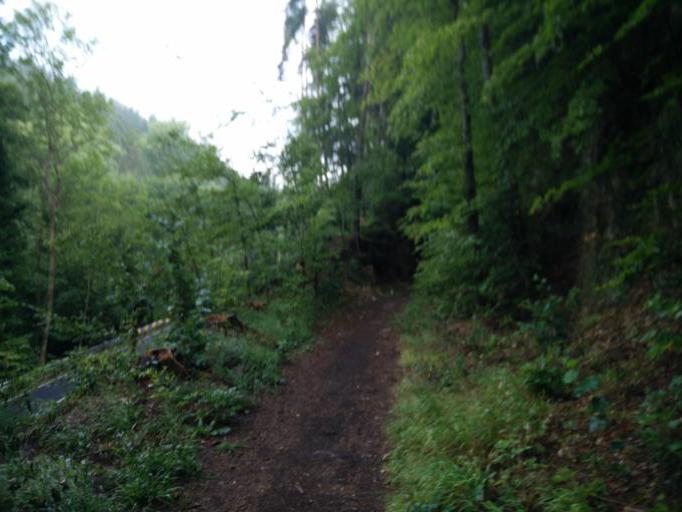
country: LU
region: Luxembourg
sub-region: Canton de Capellen
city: Mamer
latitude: 49.6392
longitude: 6.0486
